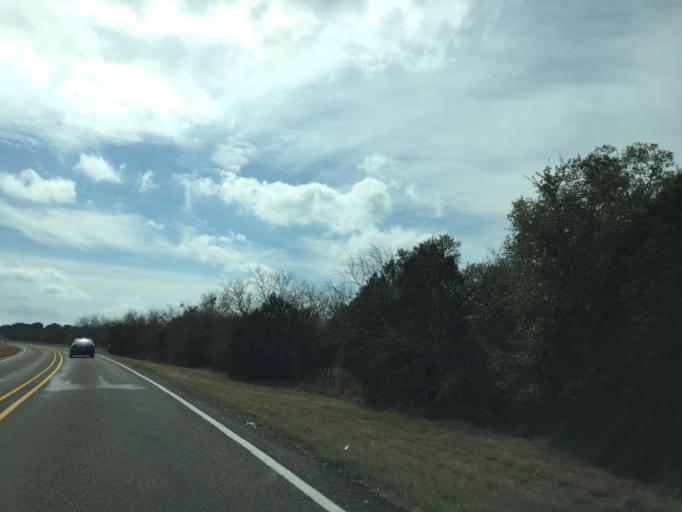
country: US
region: Texas
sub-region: Burnet County
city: Granite Shoals
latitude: 30.5059
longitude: -98.4411
